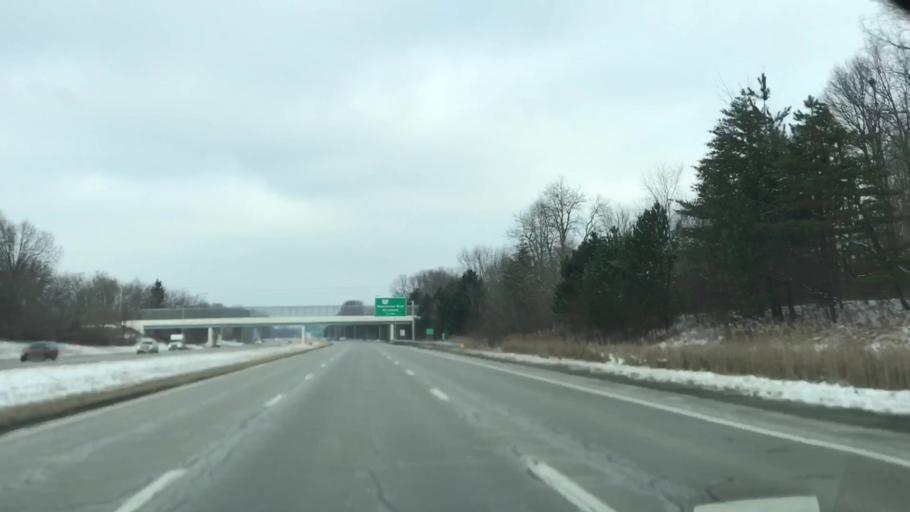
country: US
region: Ohio
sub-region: Mahoning County
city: Struthers
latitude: 41.0488
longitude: -80.6298
